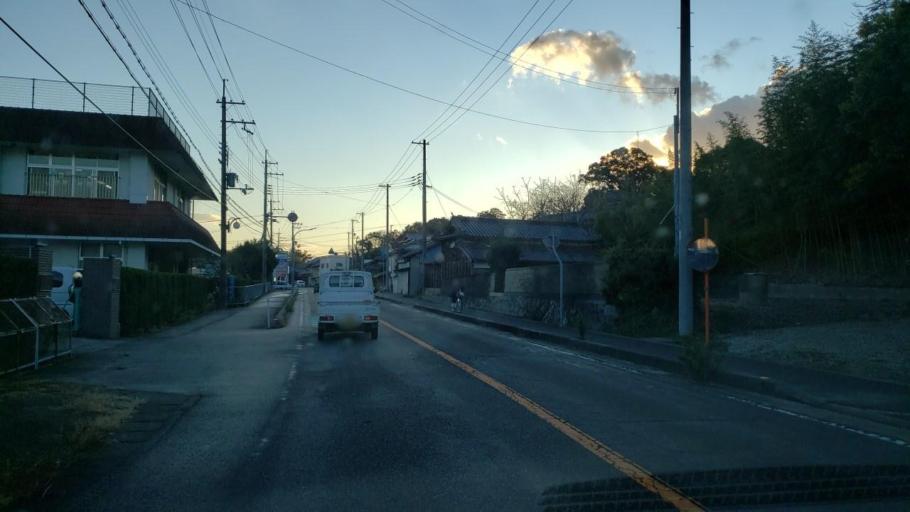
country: JP
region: Hyogo
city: Sumoto
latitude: 34.3976
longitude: 134.8135
